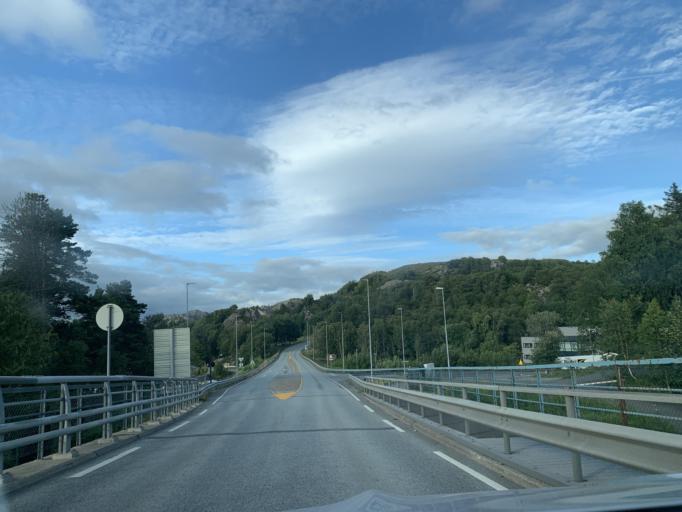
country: NO
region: Rogaland
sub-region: Eigersund
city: Egersund
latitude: 58.4615
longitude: 5.9790
